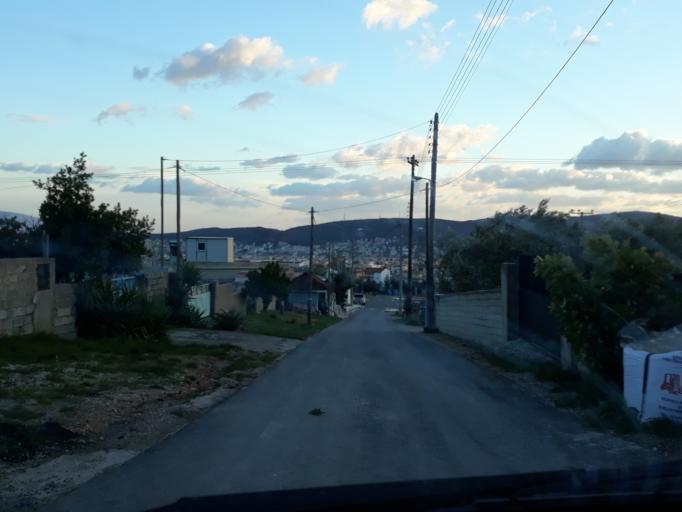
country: GR
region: Attica
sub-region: Nomarchia Dytikis Attikis
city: Ano Liosia
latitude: 38.0978
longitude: 23.6998
